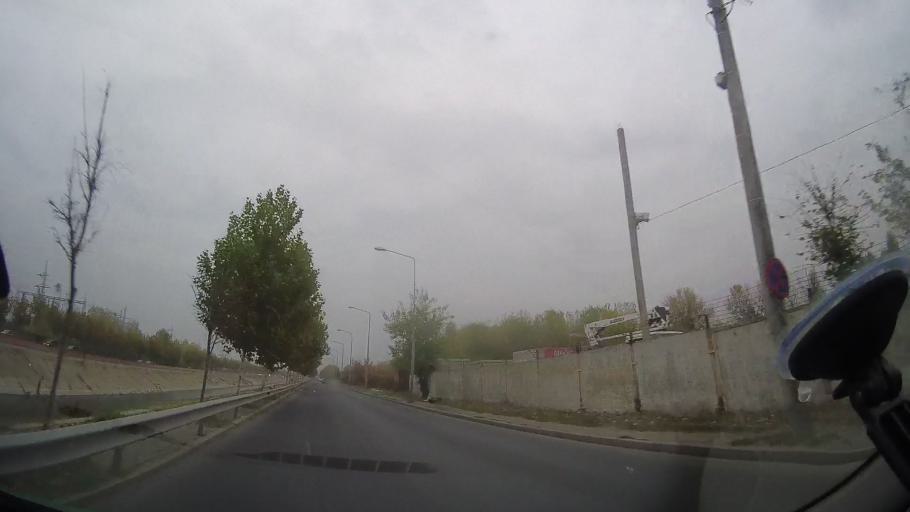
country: RO
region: Ilfov
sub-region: Comuna Popesti-Leordeni
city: Popesti-Leordeni
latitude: 44.4014
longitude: 26.1500
